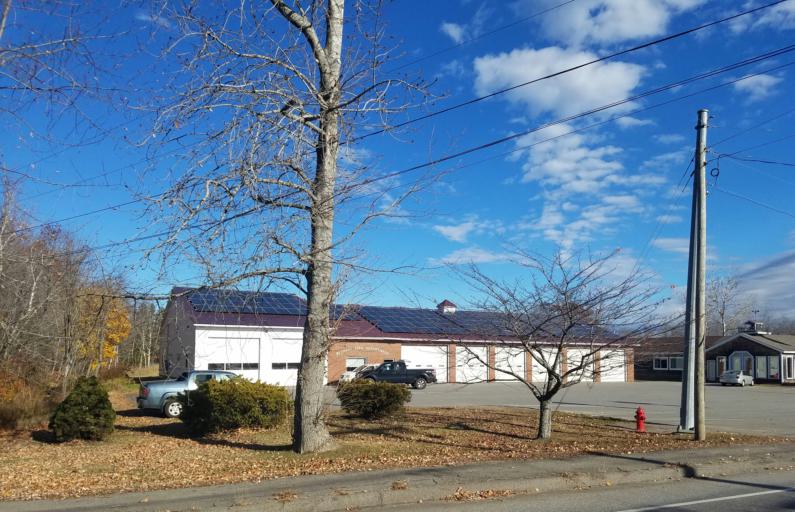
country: US
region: Maine
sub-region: Waldo County
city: Belfast
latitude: 44.4240
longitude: -69.0207
